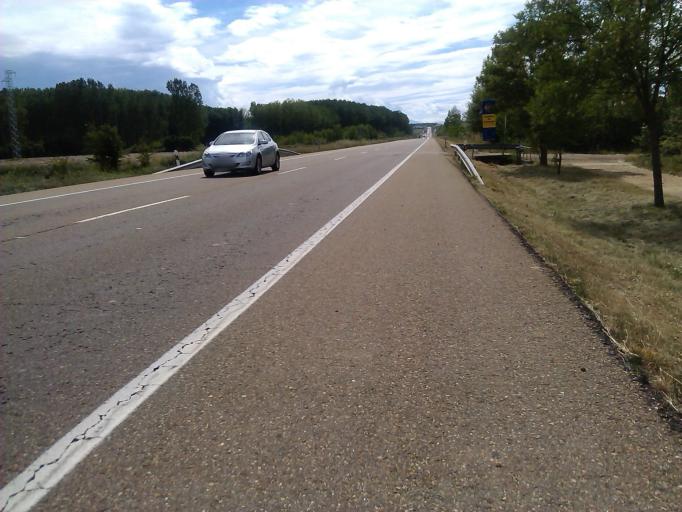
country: ES
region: Castille and Leon
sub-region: Provincia de Leon
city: Villarejo de Orbigo
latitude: 42.4551
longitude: -5.9029
